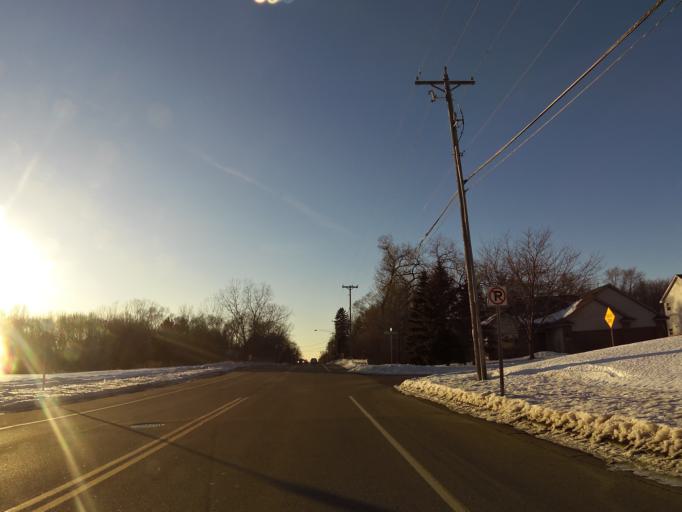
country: US
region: Minnesota
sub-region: Ramsey County
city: North Saint Paul
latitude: 45.0209
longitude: -93.0388
